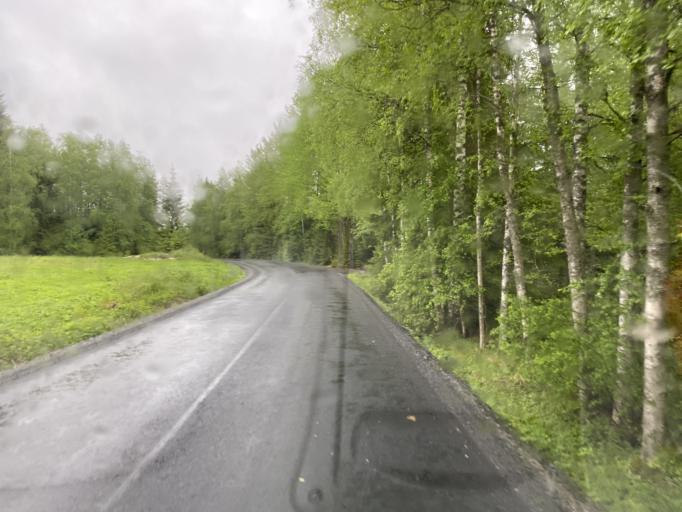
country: FI
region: Pirkanmaa
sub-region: Etelae-Pirkanmaa
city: Urjala
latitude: 60.9831
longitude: 23.4765
